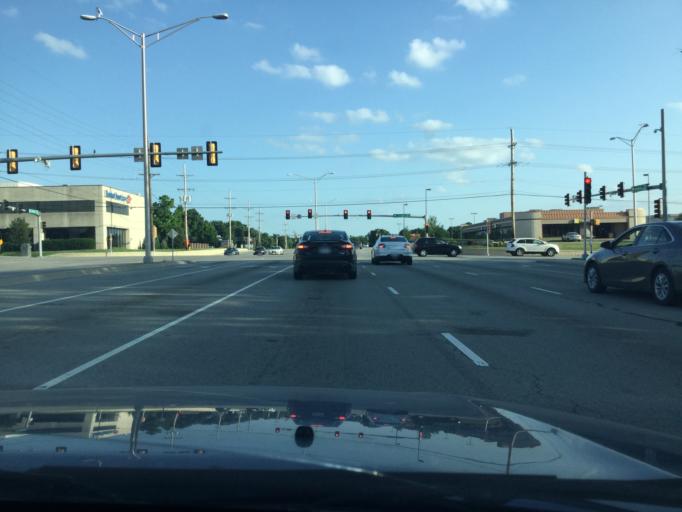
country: US
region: Kansas
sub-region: Johnson County
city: Lenexa
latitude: 38.9282
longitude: -94.6863
